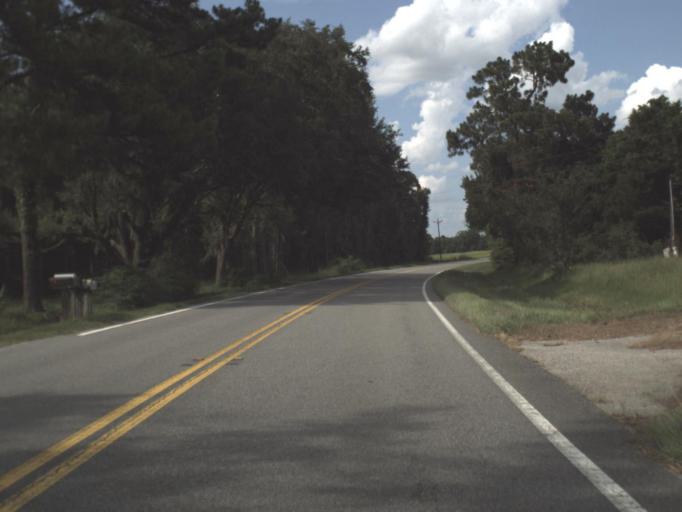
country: US
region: Florida
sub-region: Madison County
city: Madison
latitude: 30.4175
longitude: -83.6376
